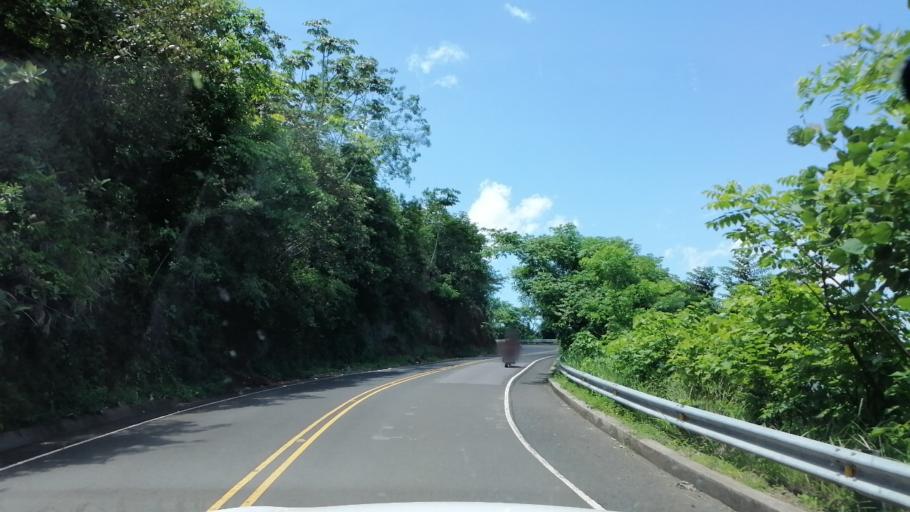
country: SV
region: San Miguel
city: Ciudad Barrios
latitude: 13.7918
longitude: -88.2899
